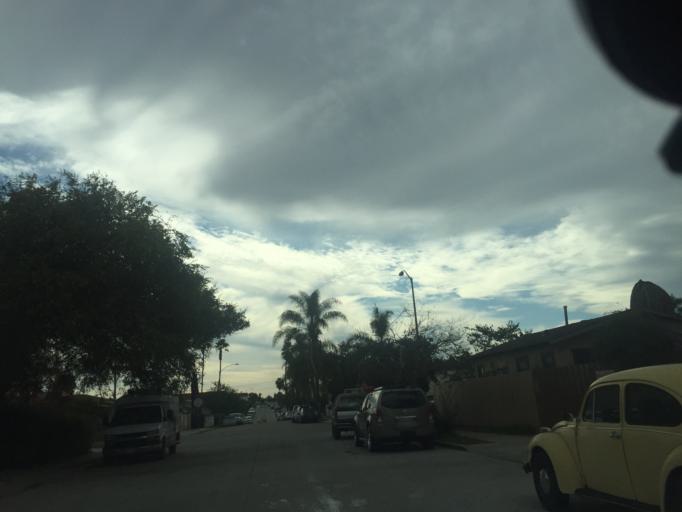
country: US
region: California
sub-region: San Diego County
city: Lemon Grove
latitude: 32.7536
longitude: -117.0912
